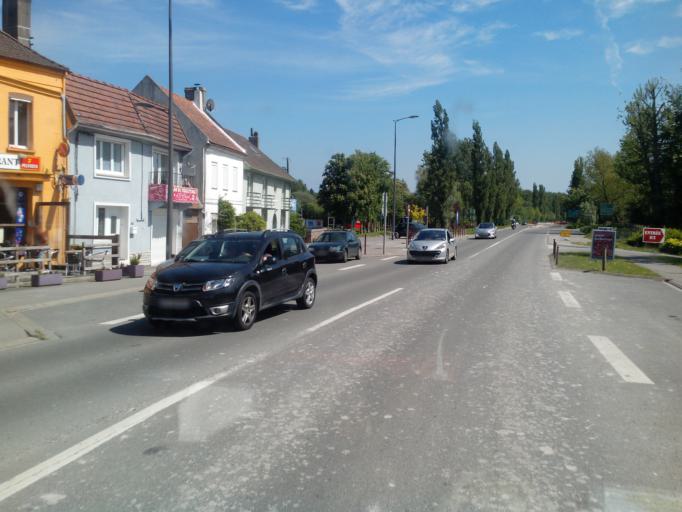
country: FR
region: Nord-Pas-de-Calais
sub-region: Departement du Pas-de-Calais
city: Montreuil
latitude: 50.4813
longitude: 1.7639
